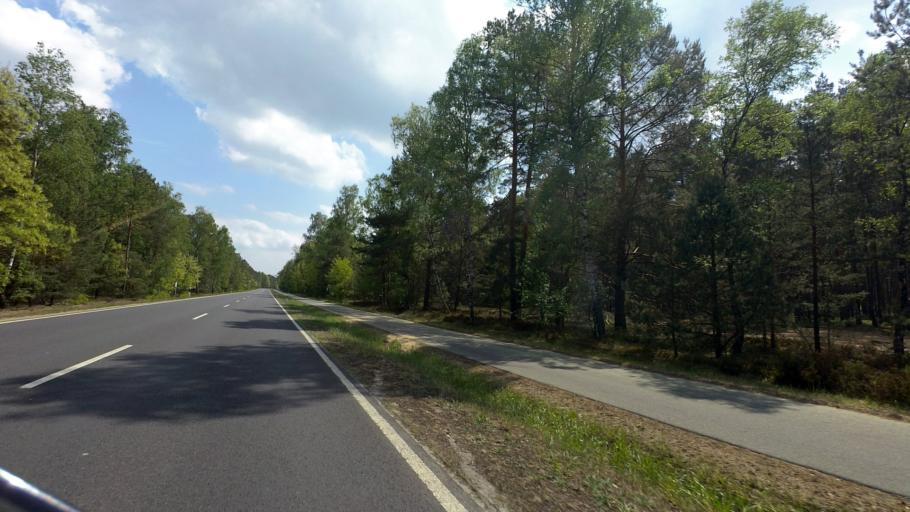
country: DE
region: Saxony
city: Rietschen
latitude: 51.4487
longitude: 14.7696
